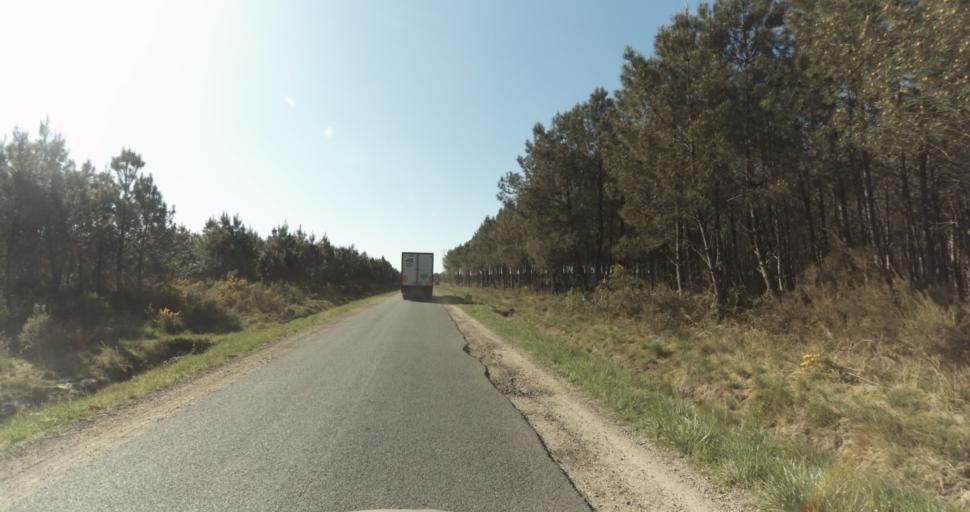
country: FR
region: Aquitaine
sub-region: Departement de la Gironde
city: Marcheprime
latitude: 44.7540
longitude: -0.8495
